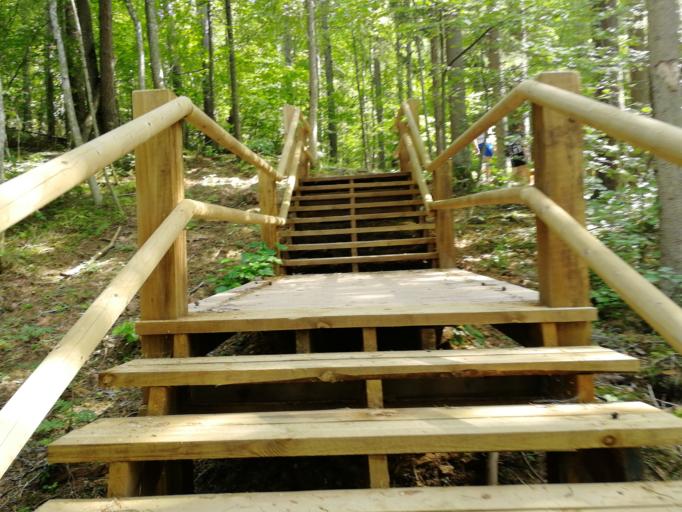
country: LV
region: Cesu Rajons
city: Cesis
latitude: 57.3014
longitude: 25.2211
